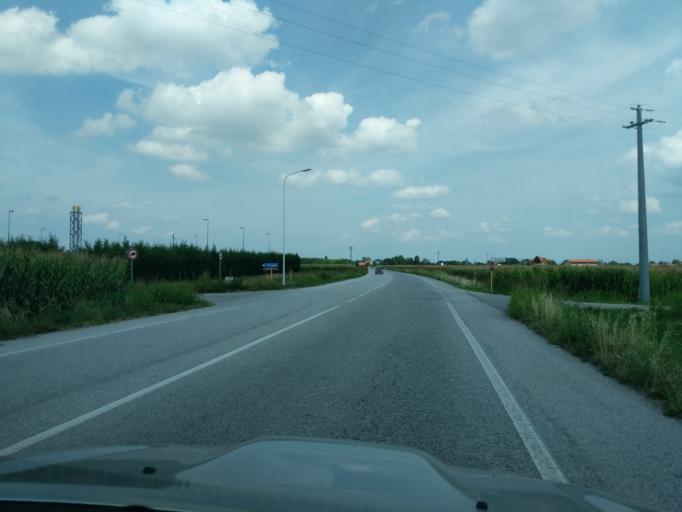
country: IT
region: Piedmont
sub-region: Provincia di Cuneo
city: Cuneo
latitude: 44.4092
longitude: 7.5927
